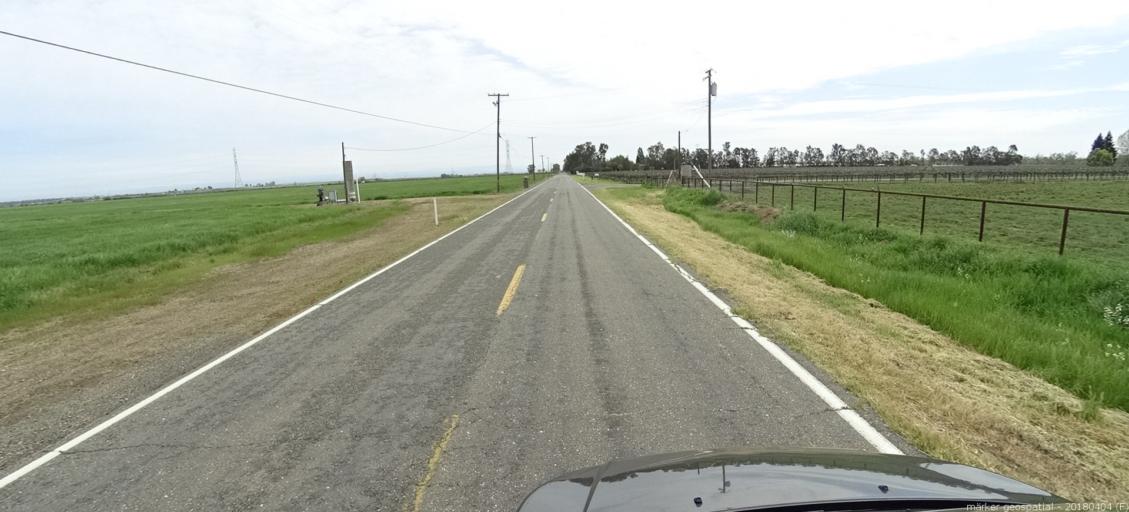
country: US
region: California
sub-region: Sacramento County
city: Herald
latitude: 38.2633
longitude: -121.1998
